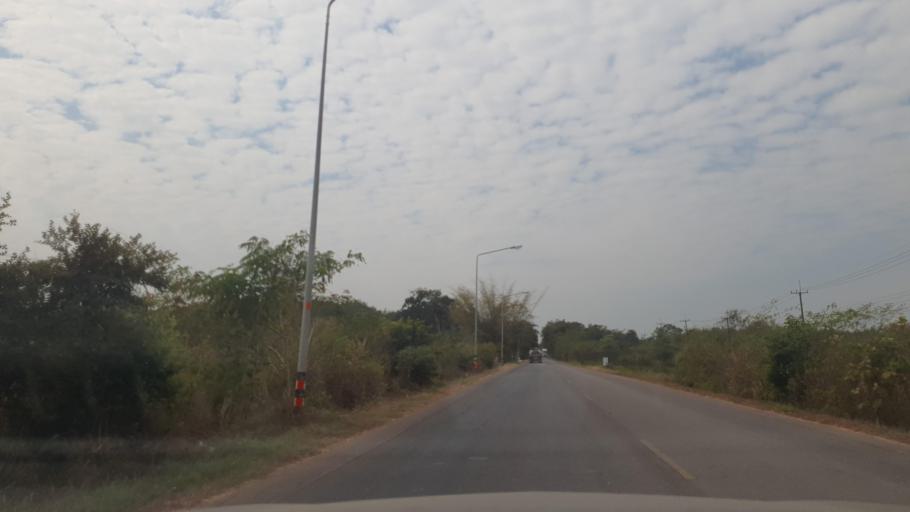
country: TH
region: Changwat Bueng Kan
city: Bung Khla
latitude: 18.3044
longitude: 103.9633
